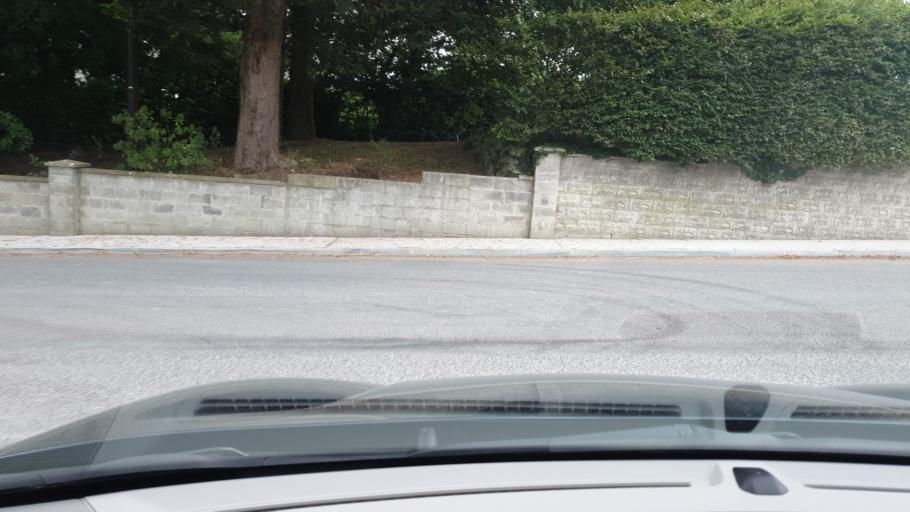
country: IE
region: Leinster
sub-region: An Mhi
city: Stamullin
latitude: 53.5874
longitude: -6.3399
